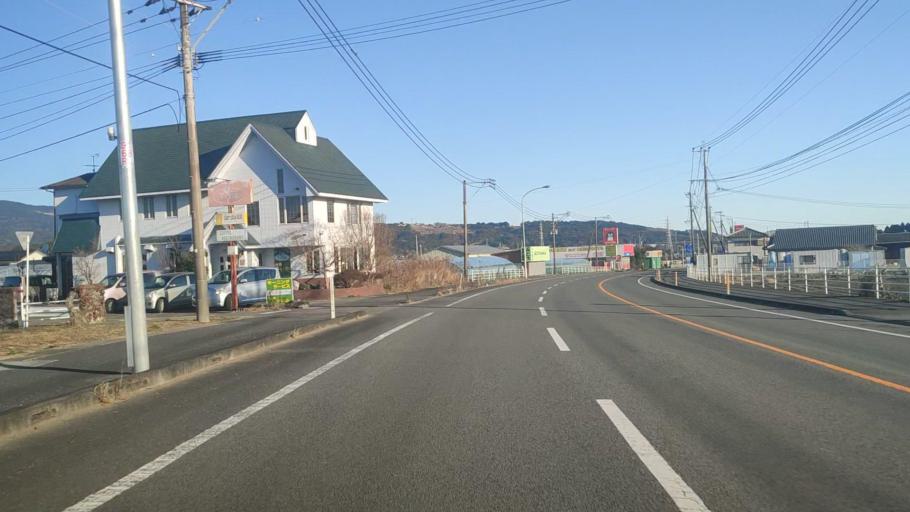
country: JP
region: Miyazaki
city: Takanabe
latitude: 32.2497
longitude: 131.5516
